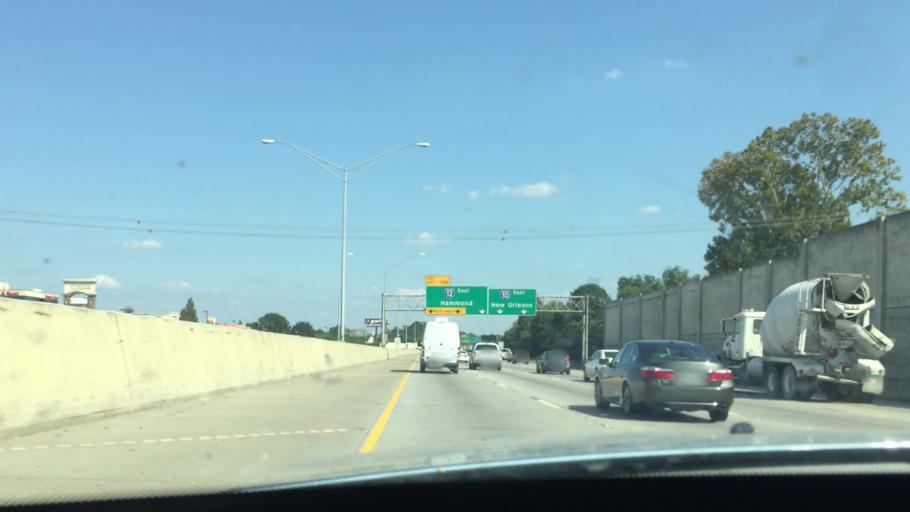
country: US
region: Louisiana
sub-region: East Baton Rouge Parish
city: Baton Rouge
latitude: 30.4221
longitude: -91.1314
